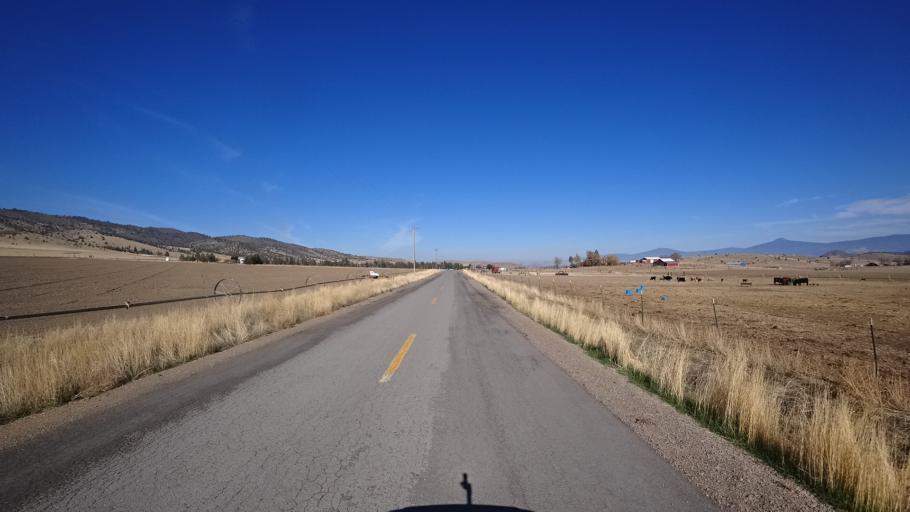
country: US
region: California
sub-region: Siskiyou County
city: Montague
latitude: 41.5767
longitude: -122.5471
